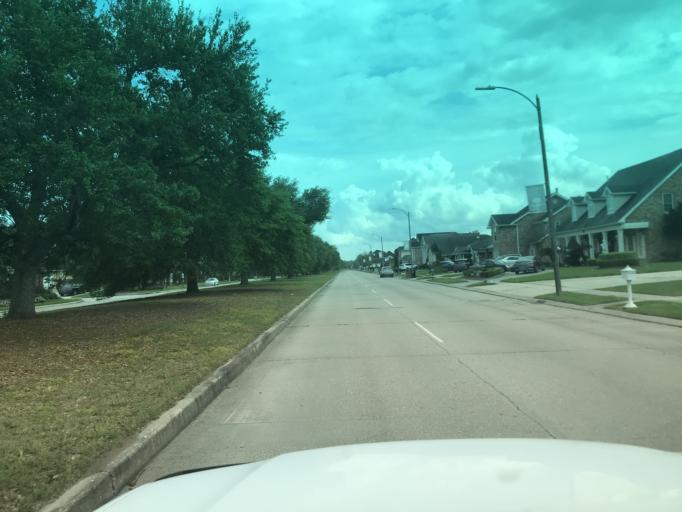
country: US
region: Louisiana
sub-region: Saint Bernard Parish
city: Chalmette
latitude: 30.0364
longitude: -89.9531
